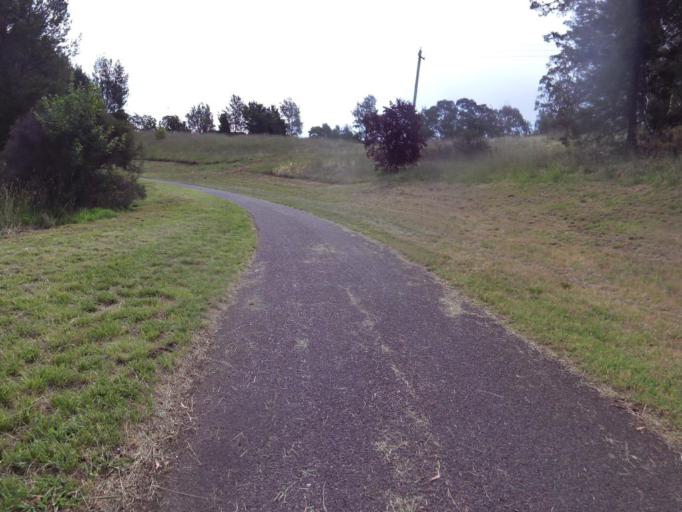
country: AU
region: Australian Capital Territory
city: Belconnen
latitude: -35.2231
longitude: 149.0794
